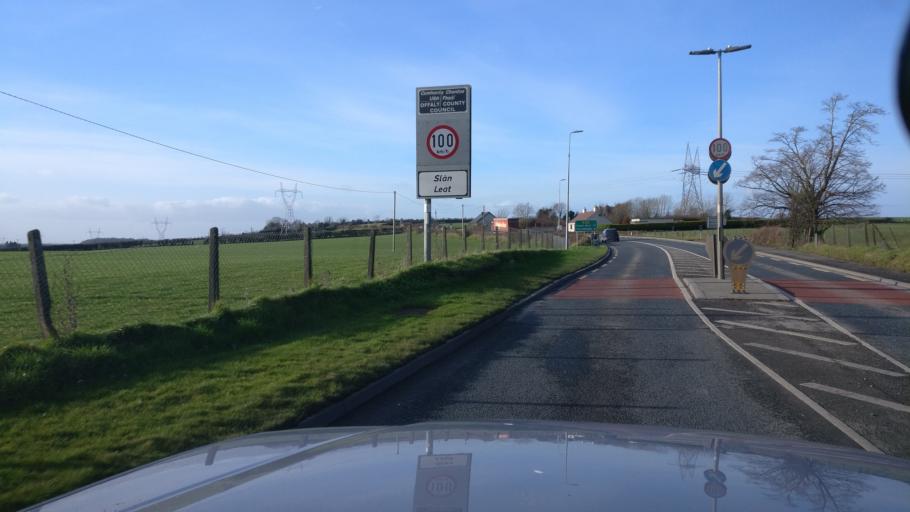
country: IE
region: Leinster
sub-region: Uibh Fhaili
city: Tullamore
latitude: 53.2153
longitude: -7.4551
